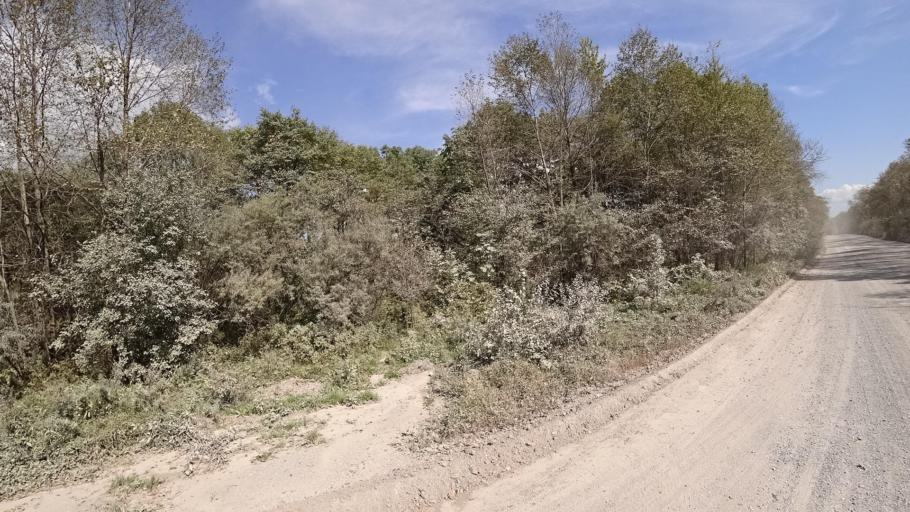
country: RU
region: Jewish Autonomous Oblast
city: Londoko
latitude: 49.0058
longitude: 131.9128
